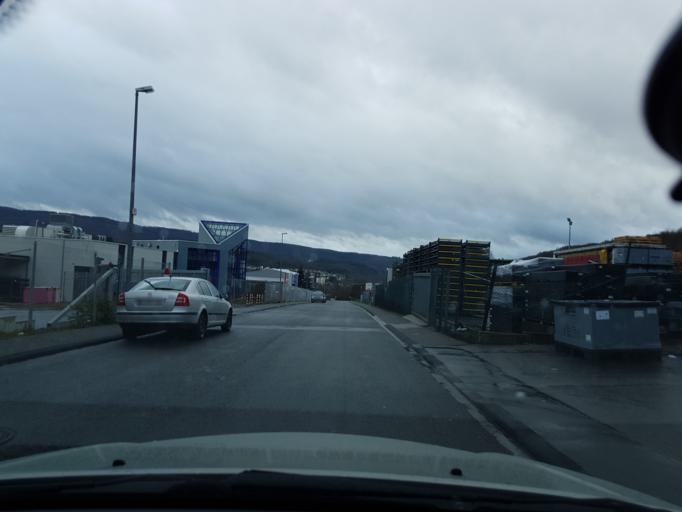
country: DE
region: Rheinland-Pfalz
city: Fischbach
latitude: 49.7257
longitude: 7.3777
